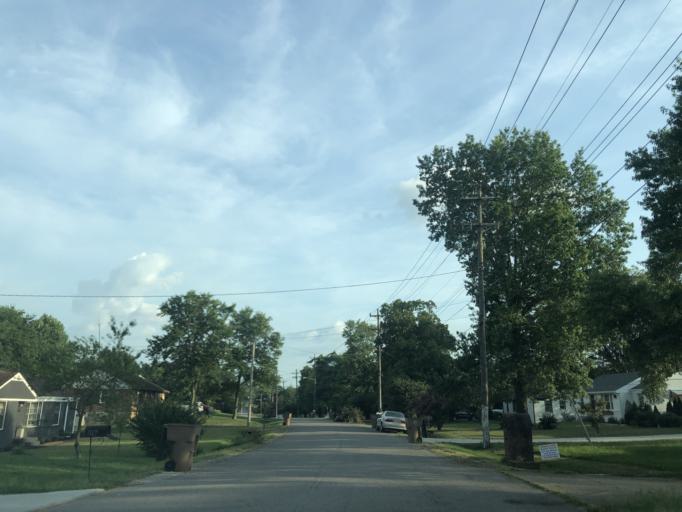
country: US
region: Tennessee
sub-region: Davidson County
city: Nashville
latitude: 36.1545
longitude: -86.6970
